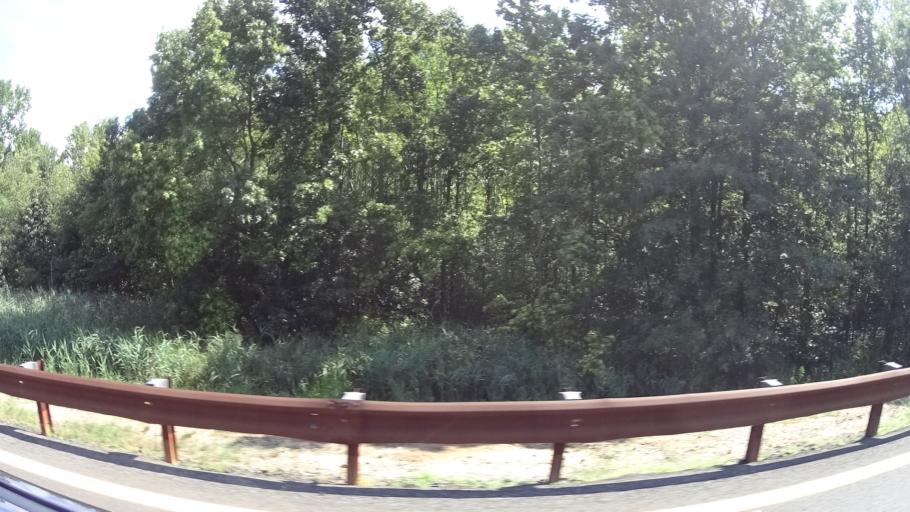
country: US
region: New Jersey
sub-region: Monmouth County
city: Keyport
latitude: 40.4135
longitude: -74.2020
